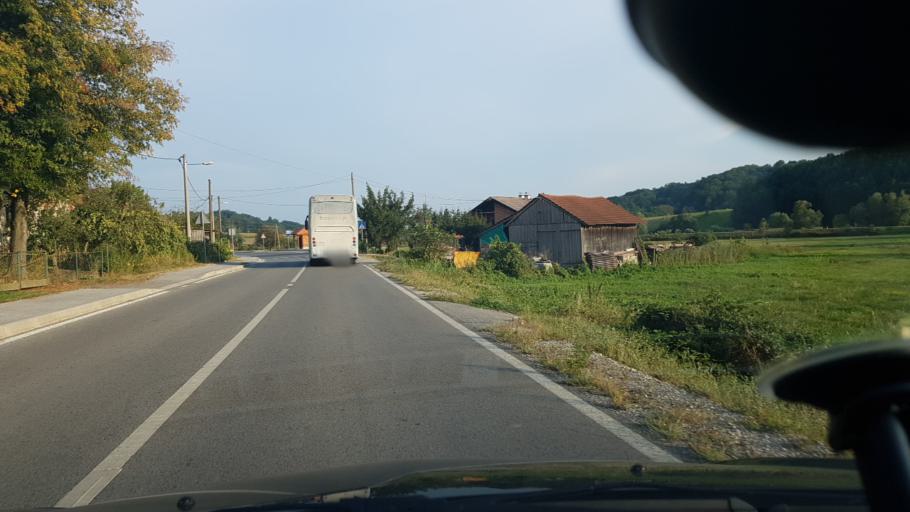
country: HR
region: Krapinsko-Zagorska
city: Pregrada
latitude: 46.1441
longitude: 15.7865
